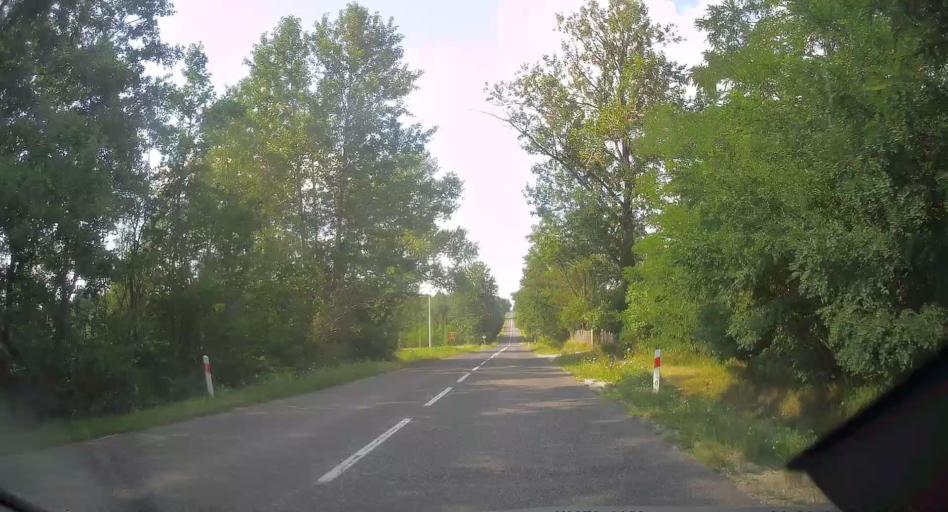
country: PL
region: Swietokrzyskie
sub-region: Powiat kielecki
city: Lopuszno
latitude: 50.9202
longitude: 20.2417
